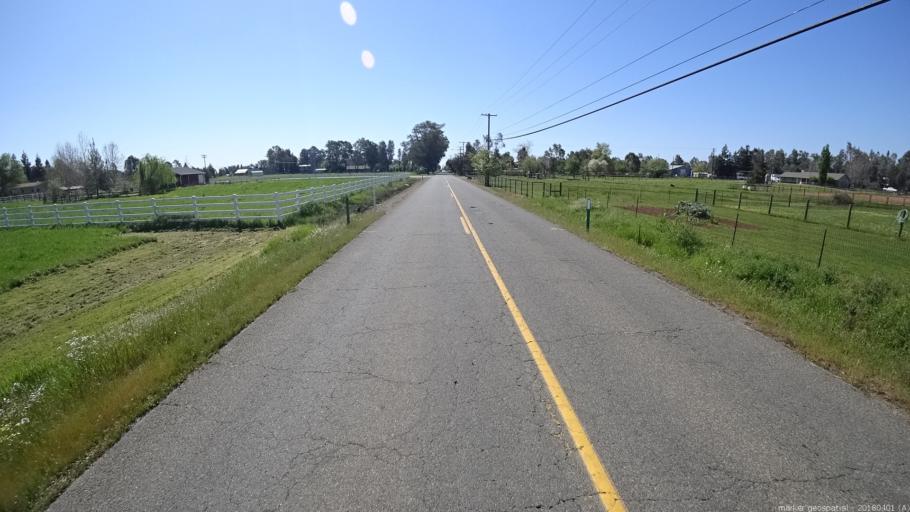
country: US
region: California
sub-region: Sacramento County
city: Wilton
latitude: 38.3880
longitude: -121.2422
